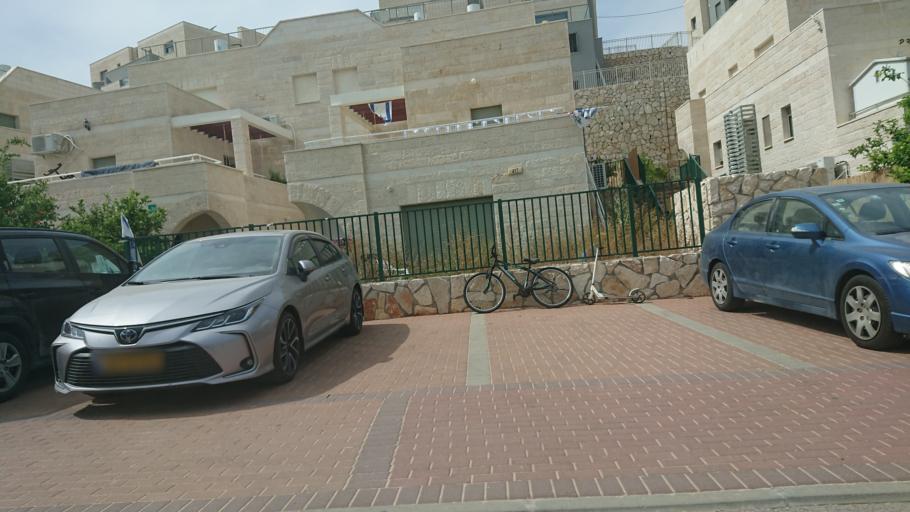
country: PS
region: West Bank
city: Rafat
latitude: 32.0625
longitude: 35.0547
